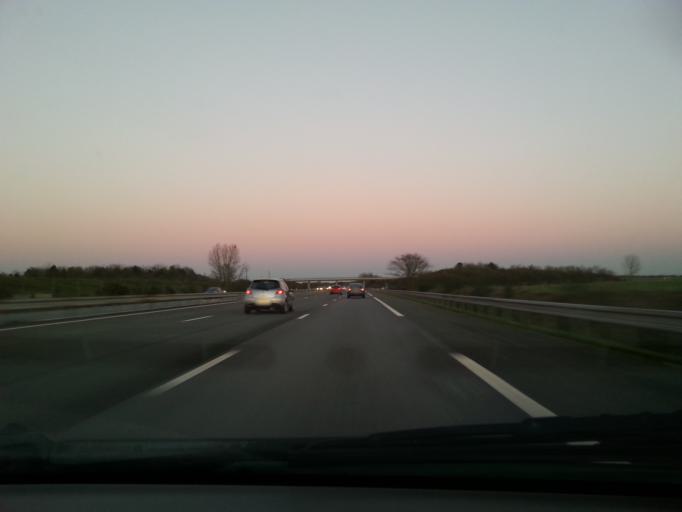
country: FR
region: Centre
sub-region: Departement d'Eure-et-Loir
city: Gallardon
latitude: 48.4855
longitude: 1.6557
